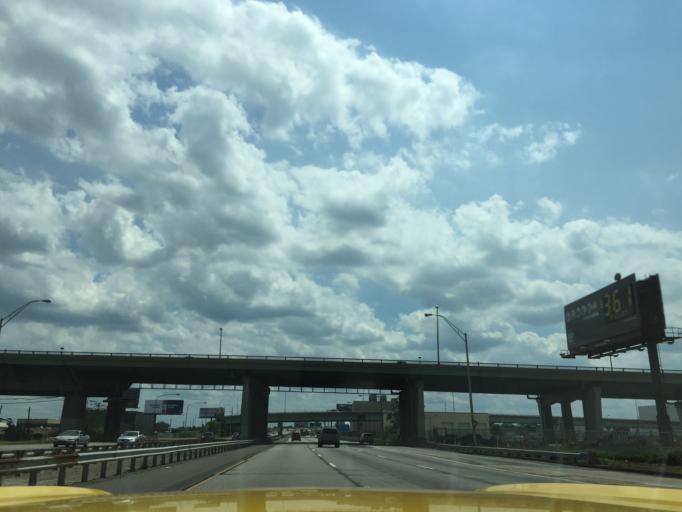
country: US
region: New Jersey
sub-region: Camden County
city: Camden
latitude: 39.9096
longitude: -75.1492
